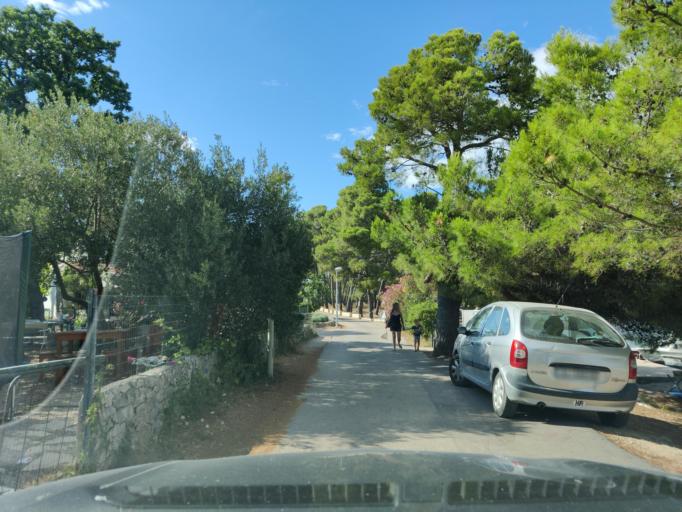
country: HR
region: Sibensko-Kniniska
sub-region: Grad Sibenik
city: Sibenik
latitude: 43.7255
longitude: 15.8473
